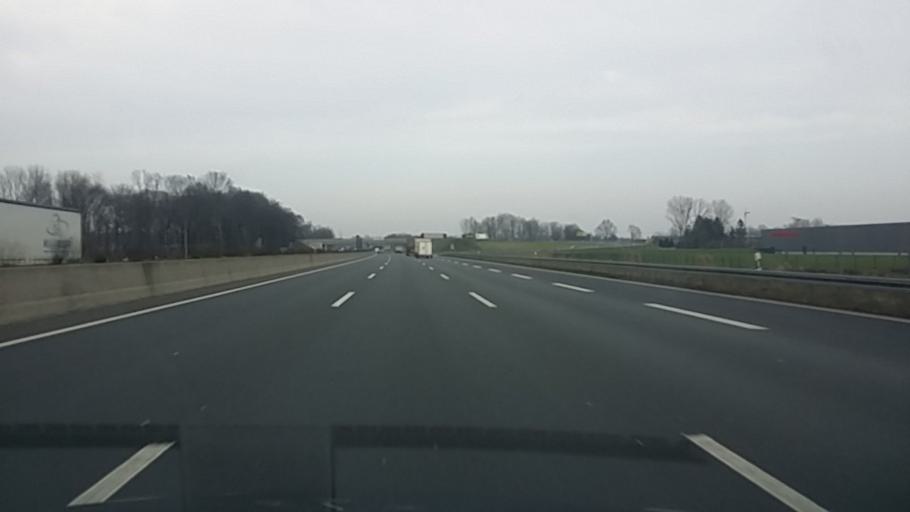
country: DE
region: North Rhine-Westphalia
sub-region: Regierungsbezirk Munster
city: Senden
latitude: 51.8833
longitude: 7.5758
